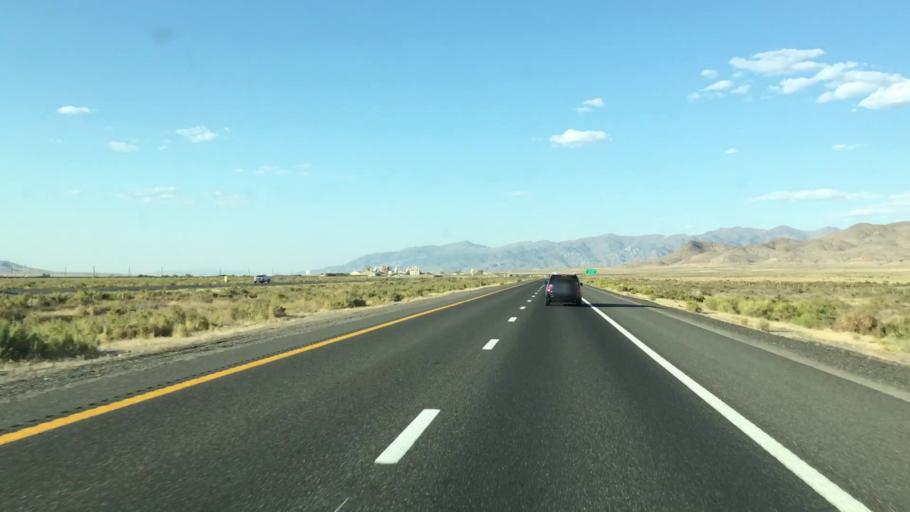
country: US
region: Nevada
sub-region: Pershing County
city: Lovelock
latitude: 40.2302
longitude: -118.3991
